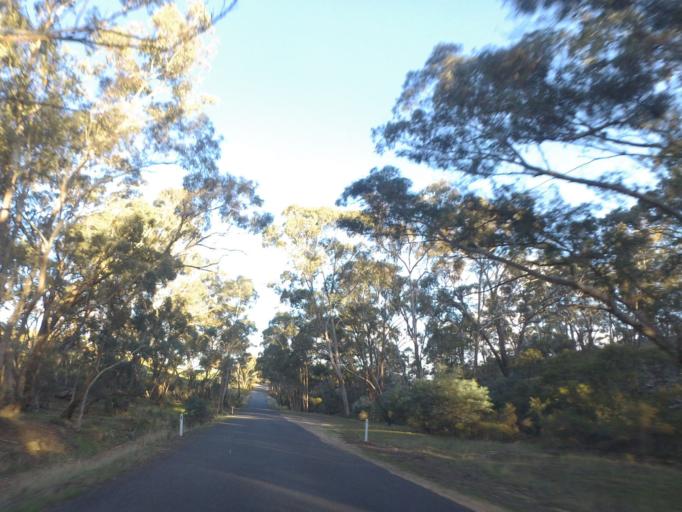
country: AU
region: Victoria
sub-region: Mount Alexander
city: Castlemaine
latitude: -37.1496
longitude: 144.2066
